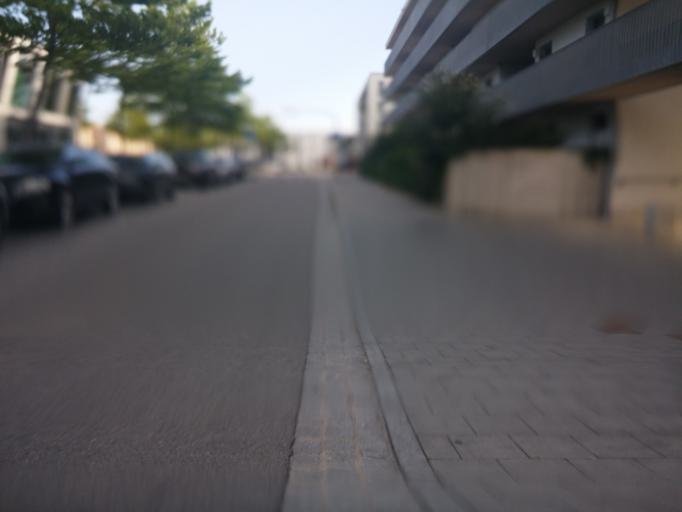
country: DE
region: Bavaria
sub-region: Upper Bavaria
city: Haar
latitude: 48.1303
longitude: 11.7055
